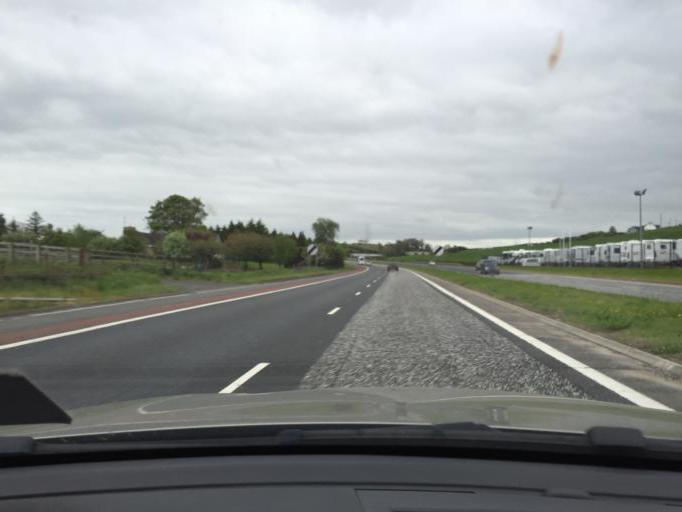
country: GB
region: Northern Ireland
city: Moira
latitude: 54.4043
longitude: -6.1685
